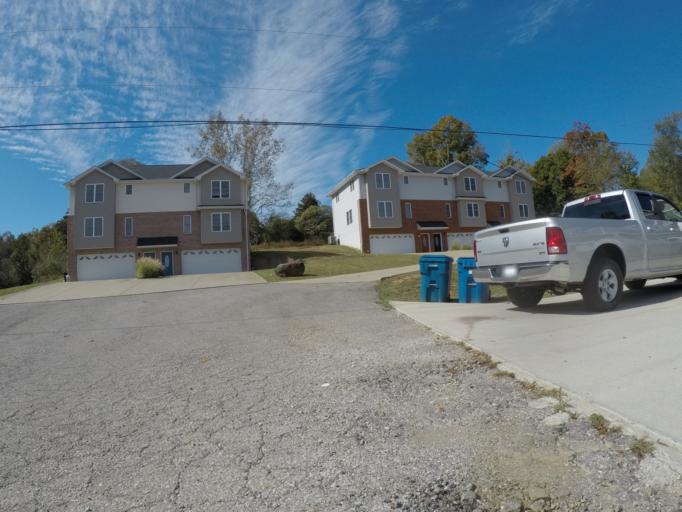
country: US
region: West Virginia
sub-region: Cabell County
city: Huntington
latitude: 38.3936
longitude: -82.3883
